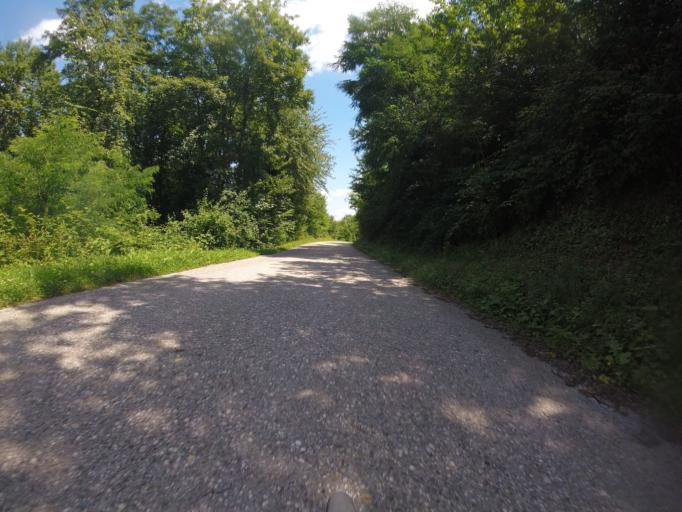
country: HR
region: Karlovacka
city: Ozalj
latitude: 45.6763
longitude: 15.4564
